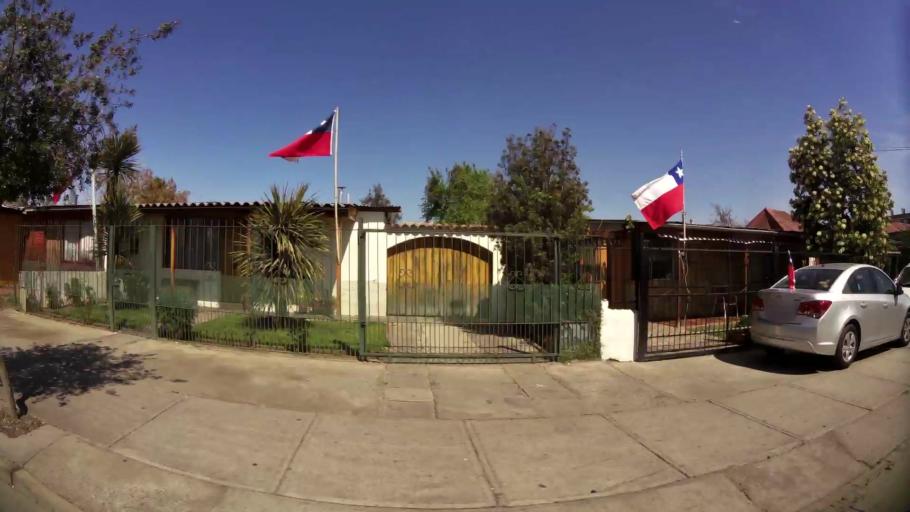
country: CL
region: Santiago Metropolitan
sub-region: Provincia de Santiago
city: Lo Prado
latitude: -33.5161
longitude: -70.7517
